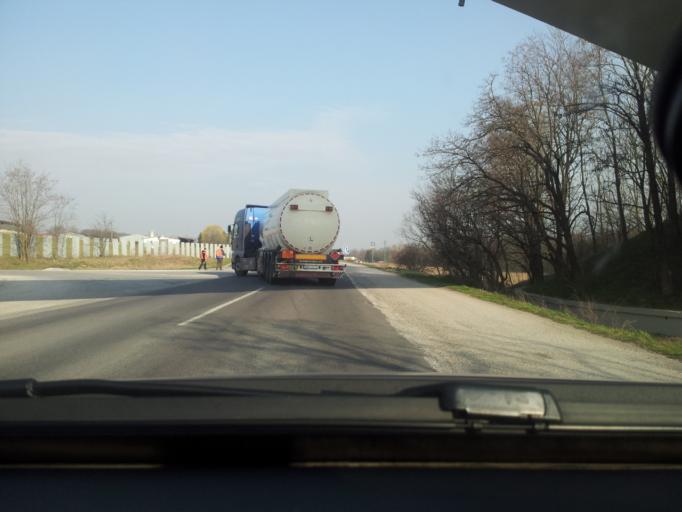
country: SK
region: Trnavsky
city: Hlohovec
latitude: 48.3822
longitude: 17.8711
